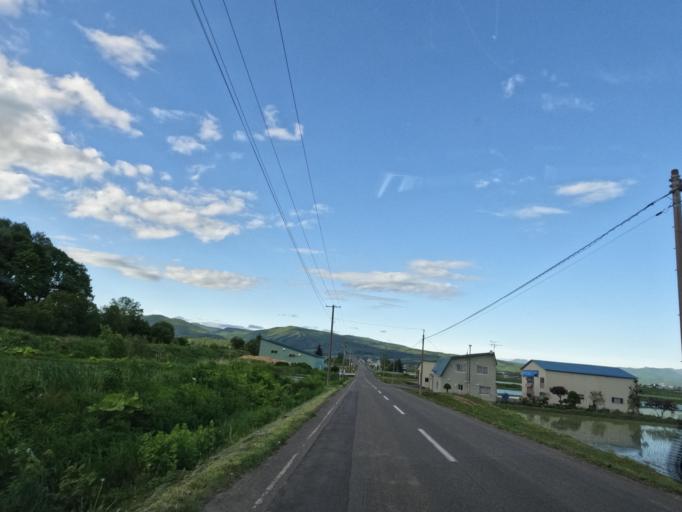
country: JP
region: Hokkaido
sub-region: Asahikawa-shi
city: Asahikawa
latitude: 43.8843
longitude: 142.4583
